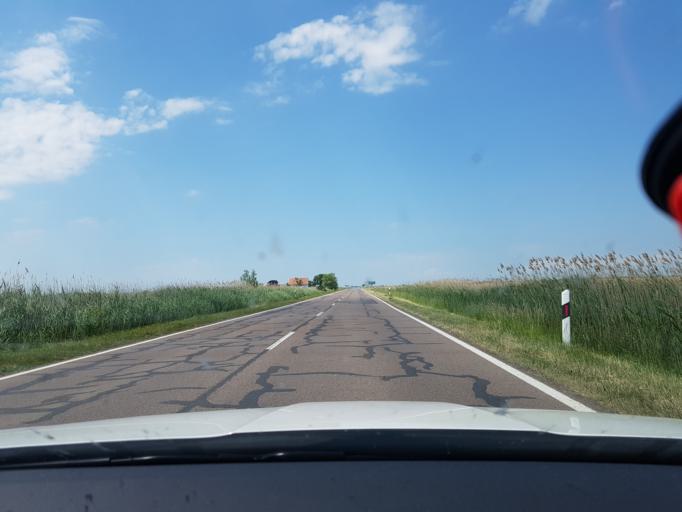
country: HU
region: Hajdu-Bihar
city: Hortobagy
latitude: 47.5900
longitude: 21.0861
